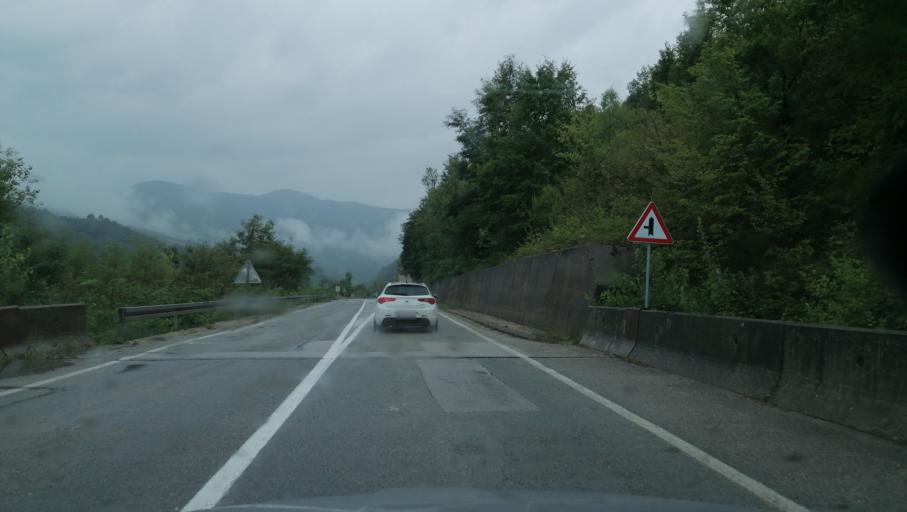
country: BA
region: Republika Srpska
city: Visegrad
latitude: 43.7240
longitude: 19.1683
